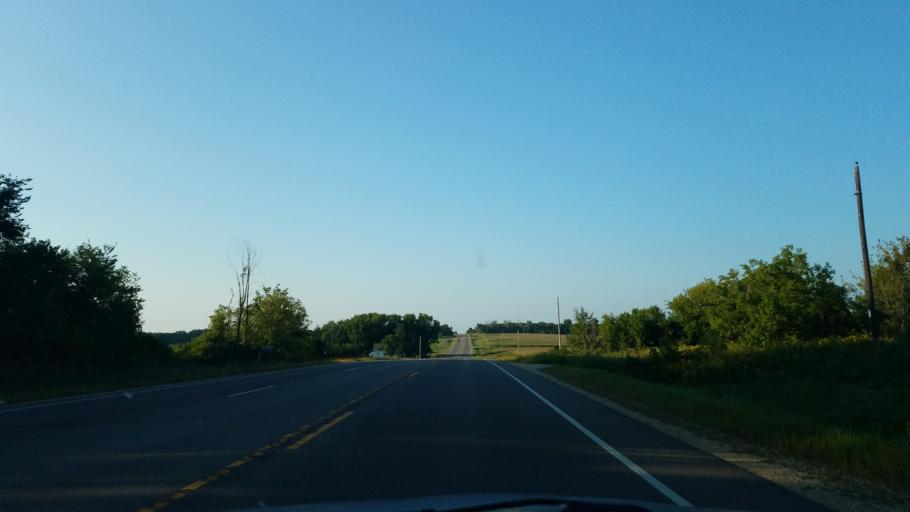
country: US
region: Wisconsin
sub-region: Saint Croix County
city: Baldwin
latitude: 45.1030
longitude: -92.3754
